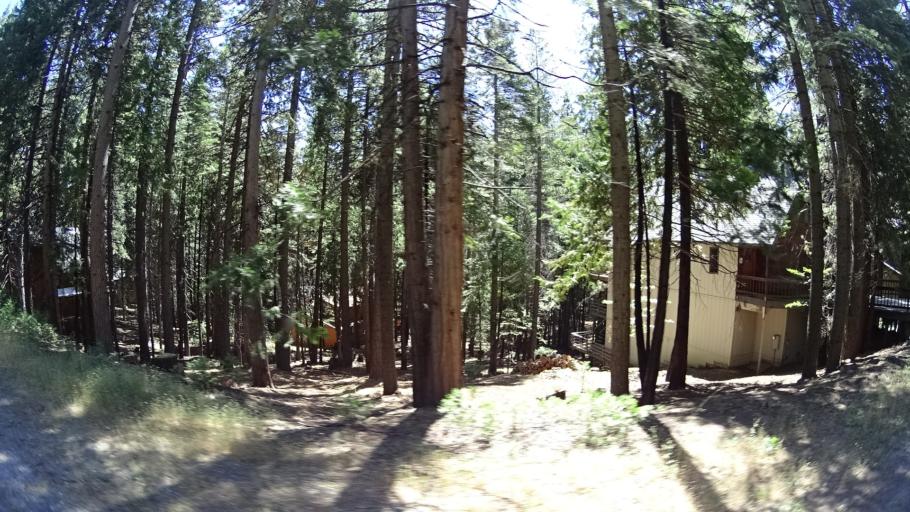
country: US
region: California
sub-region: Calaveras County
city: Arnold
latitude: 38.2907
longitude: -120.2860
